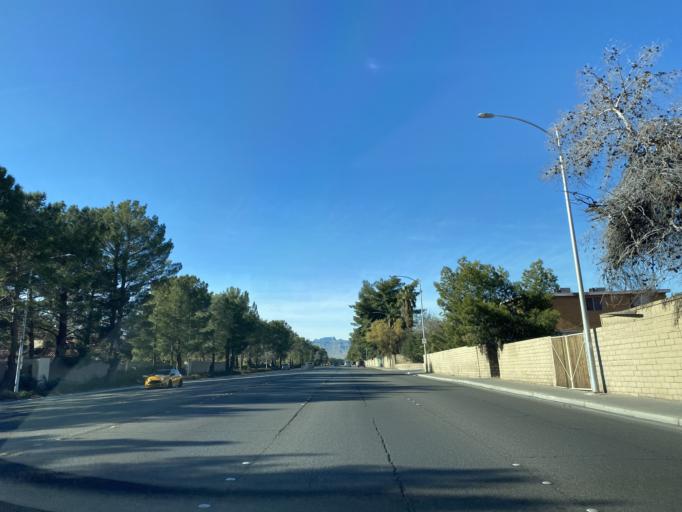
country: US
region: Nevada
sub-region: Clark County
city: Spring Valley
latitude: 36.0998
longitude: -115.2464
